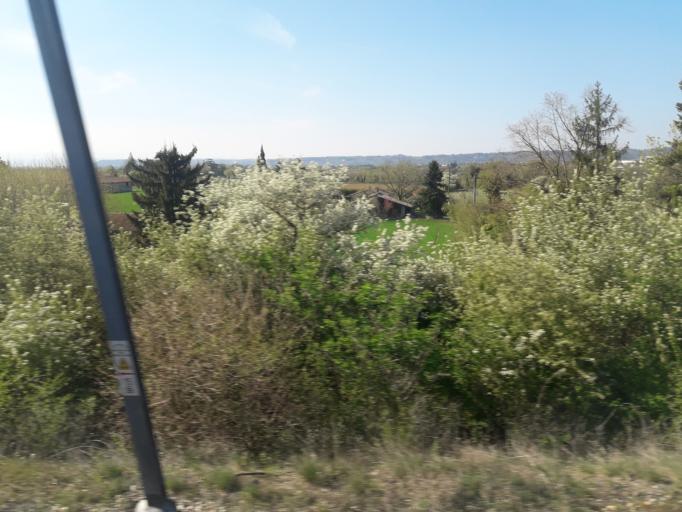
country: FR
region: Rhone-Alpes
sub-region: Departement de la Drome
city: Romans-sur-Isere
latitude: 45.0258
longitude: 5.0244
